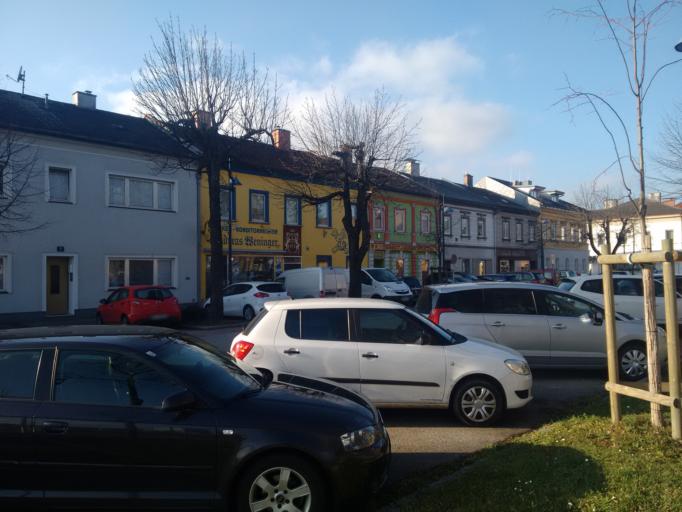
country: AT
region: Upper Austria
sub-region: Wels Stadt
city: Wels
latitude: 48.1662
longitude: 14.0240
